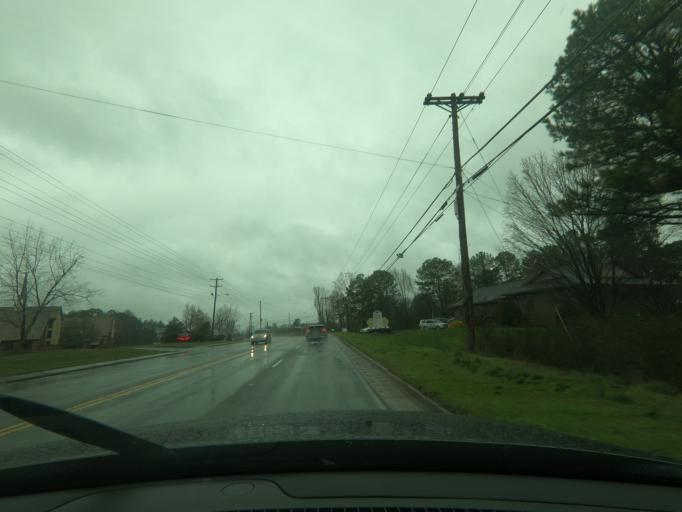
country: US
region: Georgia
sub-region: Gordon County
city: Calhoun
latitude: 34.5129
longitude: -84.9288
